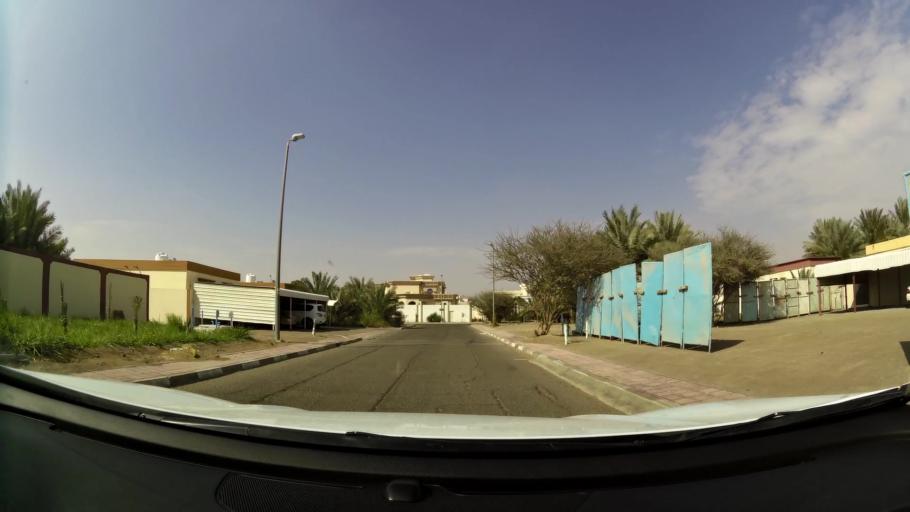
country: AE
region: Abu Dhabi
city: Al Ain
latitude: 24.0979
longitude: 55.9176
